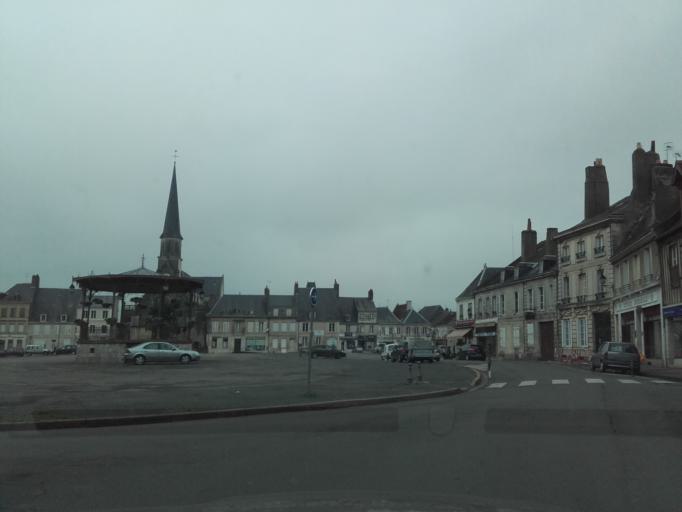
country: FR
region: Centre
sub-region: Departement du Loir-et-Cher
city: Montoire-sur-le-Loir
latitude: 47.7523
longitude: 0.8607
